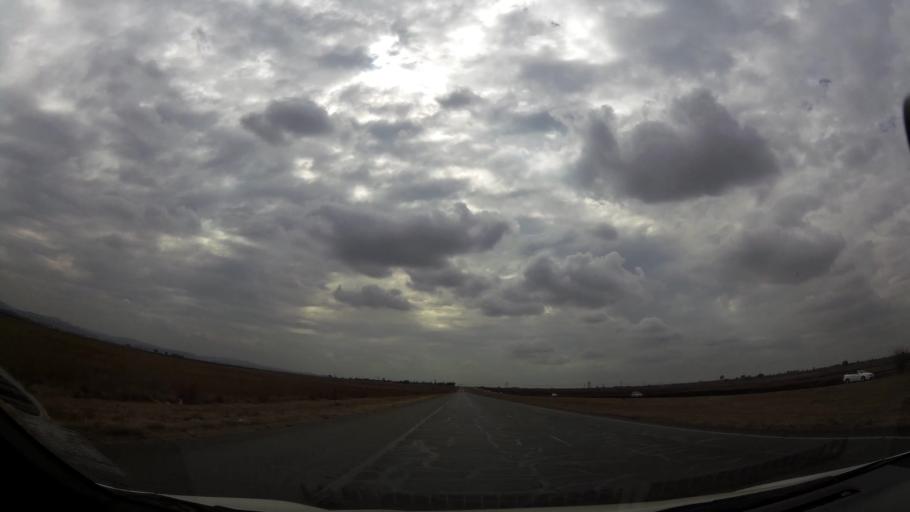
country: ZA
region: Gauteng
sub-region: Ekurhuleni Metropolitan Municipality
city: Germiston
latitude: -26.3728
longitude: 28.0910
